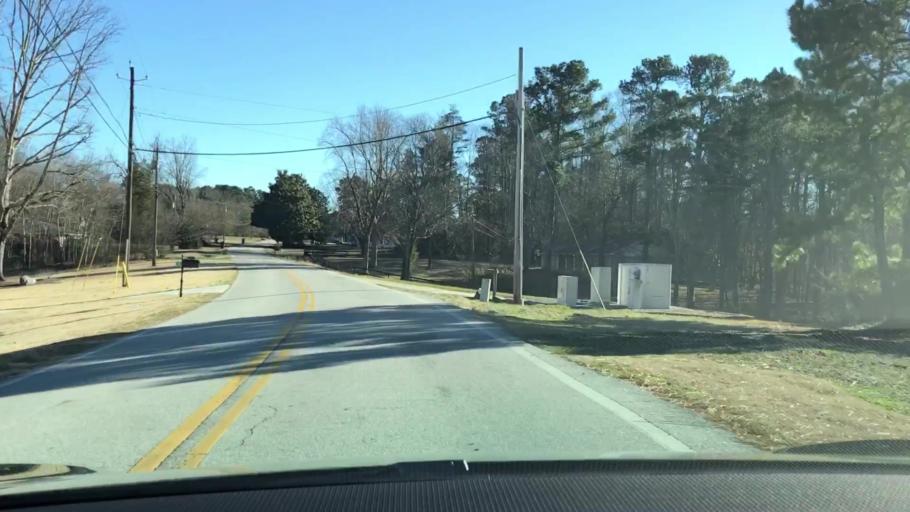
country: US
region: Georgia
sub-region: Gwinnett County
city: Buford
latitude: 34.1460
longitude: -84.0118
